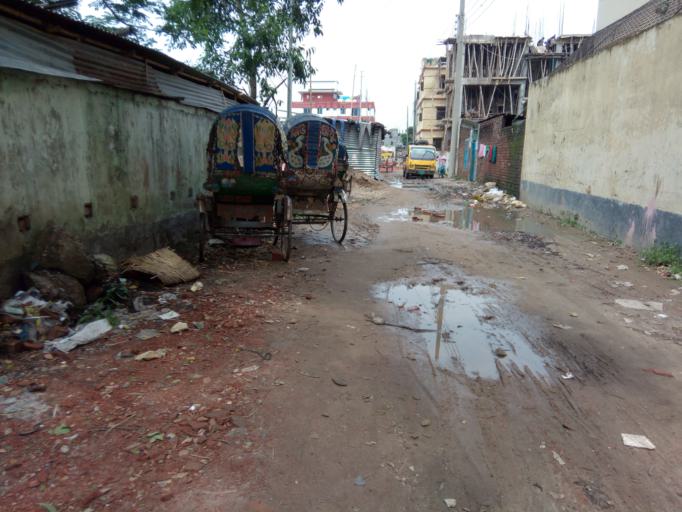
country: BD
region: Dhaka
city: Azimpur
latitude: 23.7583
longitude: 90.3442
